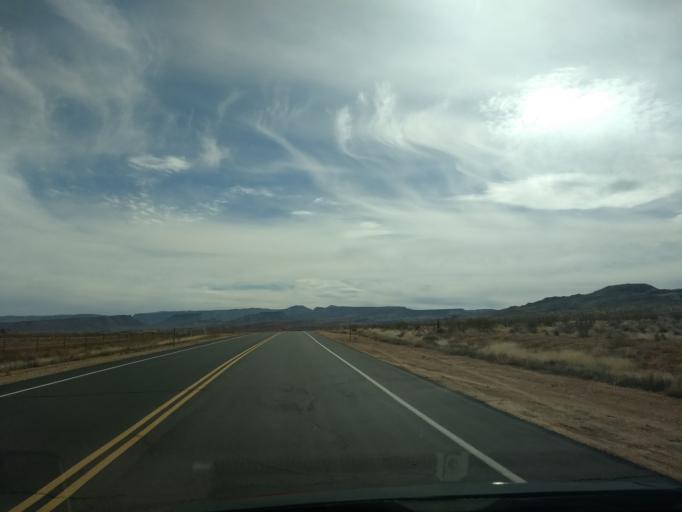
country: US
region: Utah
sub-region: Washington County
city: Washington
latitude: 37.0218
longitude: -113.5042
